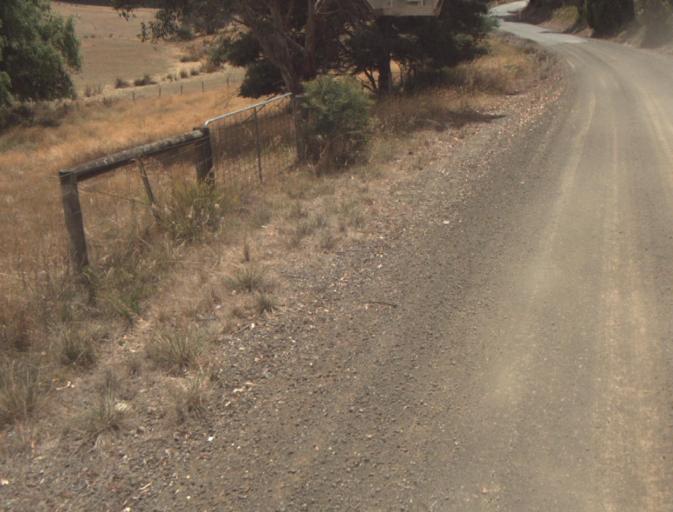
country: AU
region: Tasmania
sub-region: Launceston
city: Mayfield
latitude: -41.2161
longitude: 147.1401
